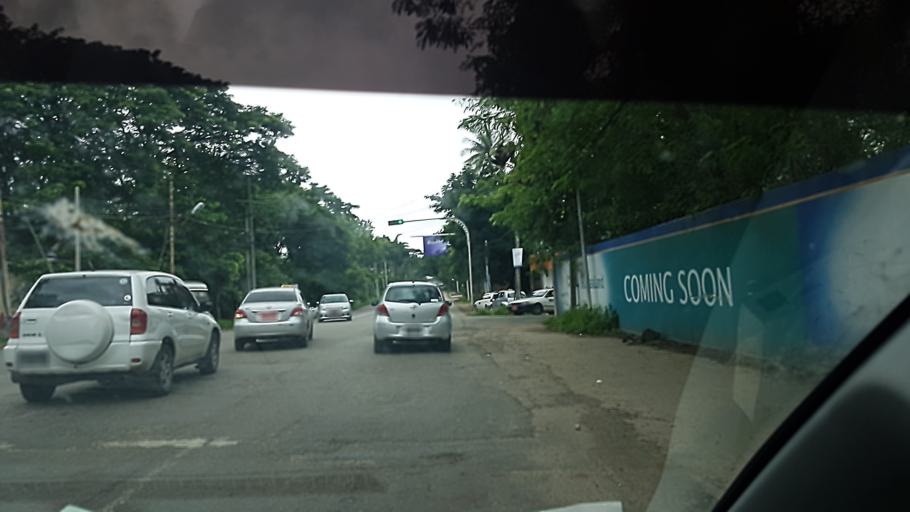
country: MM
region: Yangon
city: Yangon
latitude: 16.7969
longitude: 96.1312
